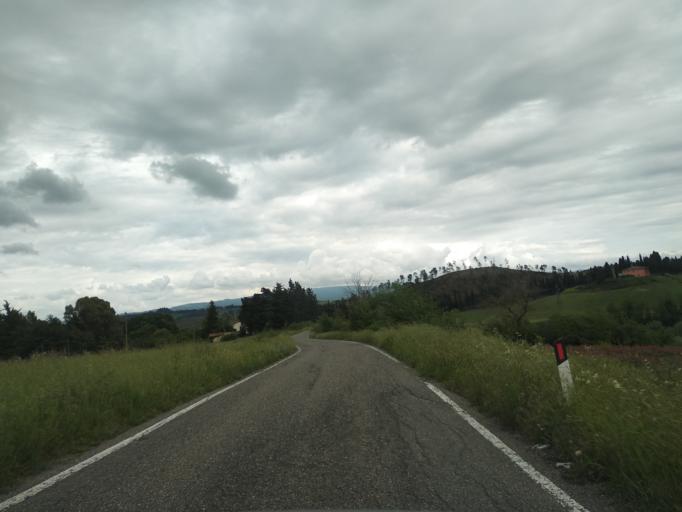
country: IT
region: Tuscany
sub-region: Provincia di Livorno
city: Collesalvetti
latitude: 43.5412
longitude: 10.4516
